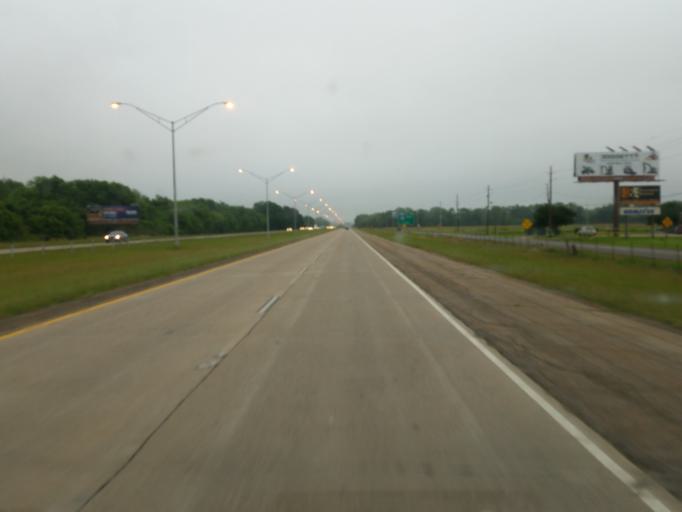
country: US
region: Louisiana
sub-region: Bossier Parish
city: Red Chute
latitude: 32.5334
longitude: -93.6545
